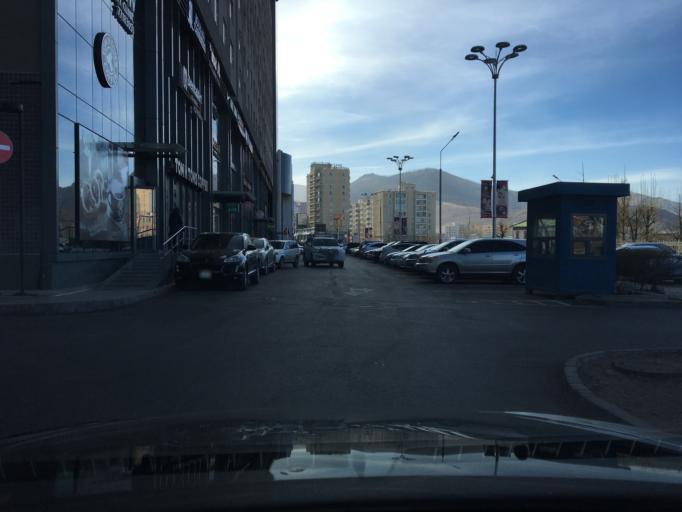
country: MN
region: Ulaanbaatar
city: Ulaanbaatar
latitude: 47.8985
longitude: 106.9092
